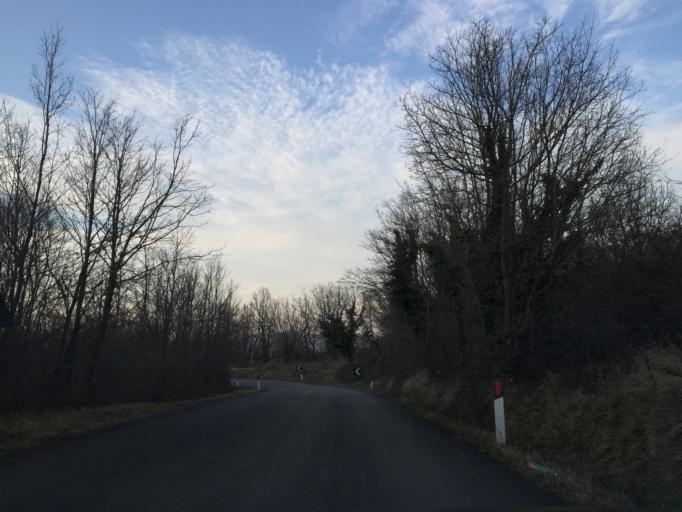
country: IT
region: Molise
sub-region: Provincia di Campobasso
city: Guardiaregia
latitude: 41.4450
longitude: 14.5503
